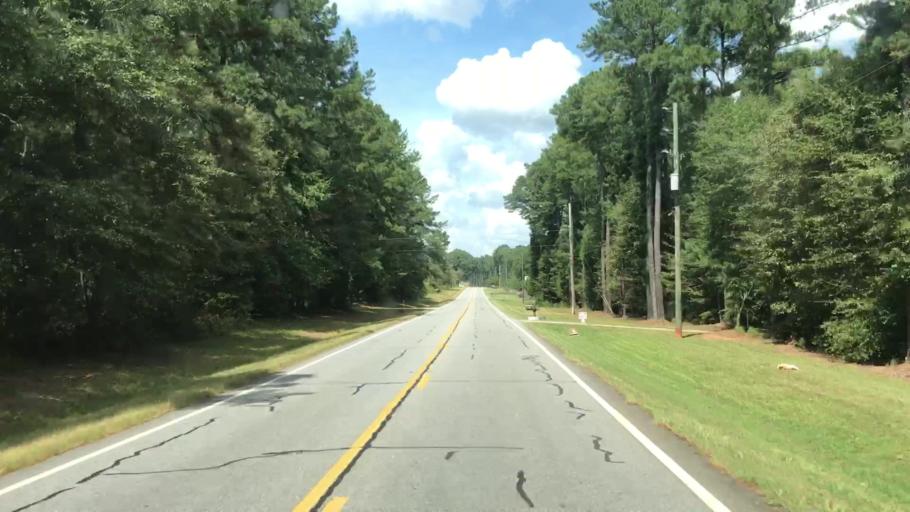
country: US
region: Georgia
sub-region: Oconee County
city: Watkinsville
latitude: 33.7833
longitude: -83.3136
